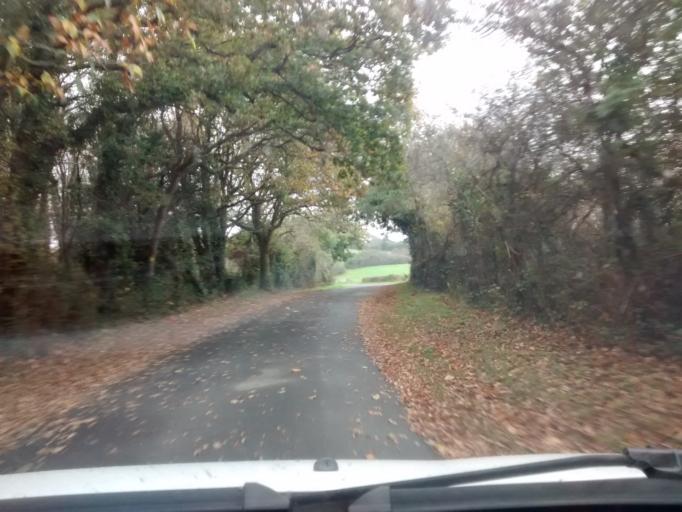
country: FR
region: Lower Normandy
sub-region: Departement de la Manche
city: Jullouville
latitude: 48.7427
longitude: -1.5640
